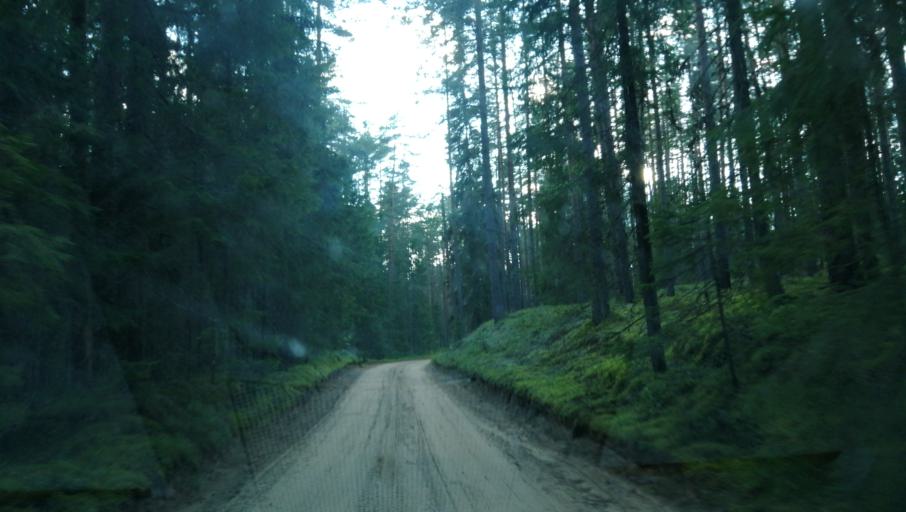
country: LV
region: Cesu Rajons
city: Cesis
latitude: 57.2904
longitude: 25.1915
